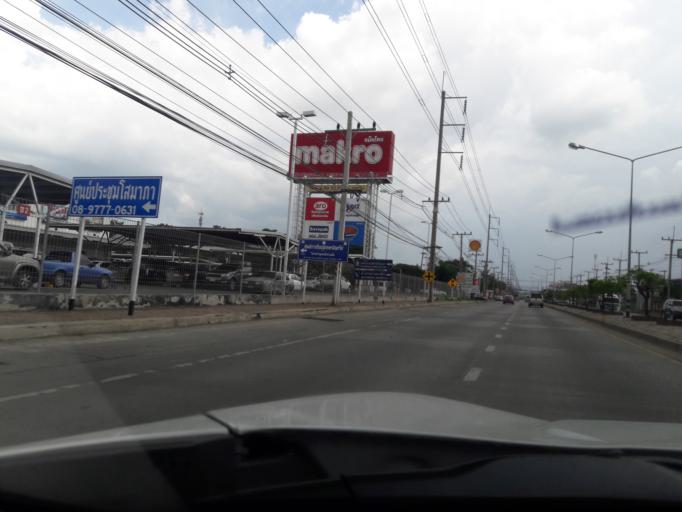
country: TH
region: Lop Buri
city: Lop Buri
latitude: 14.7819
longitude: 100.6865
